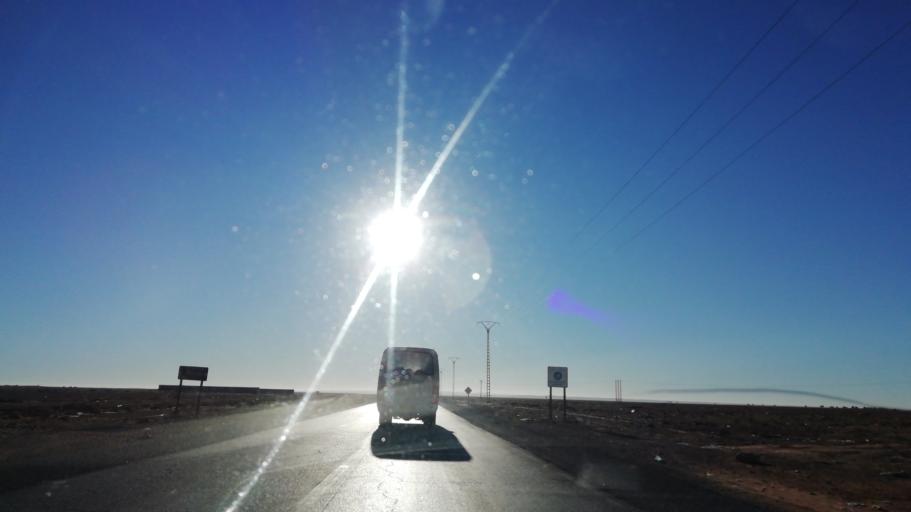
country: DZ
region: Saida
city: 'Ain el Hadjar
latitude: 34.0214
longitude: 0.1033
